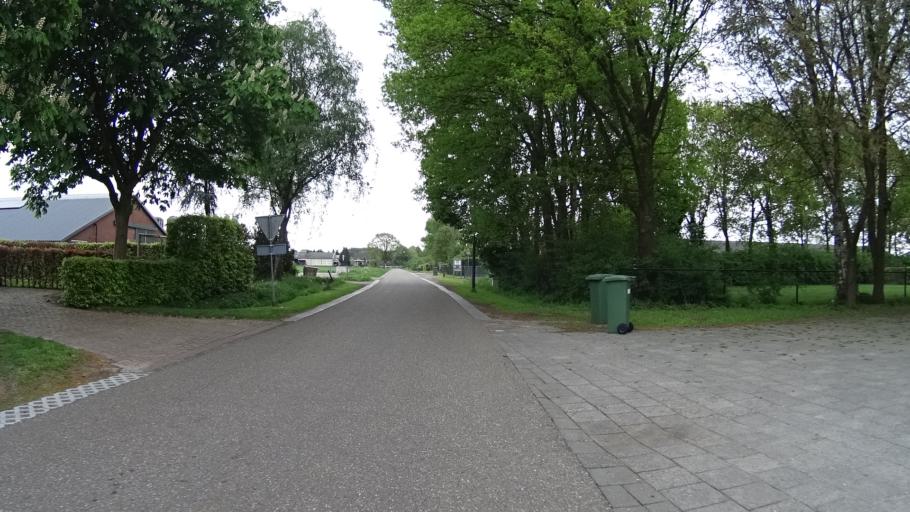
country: NL
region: North Brabant
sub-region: Gemeente Boekel
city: Boekel
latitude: 51.5924
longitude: 5.6803
